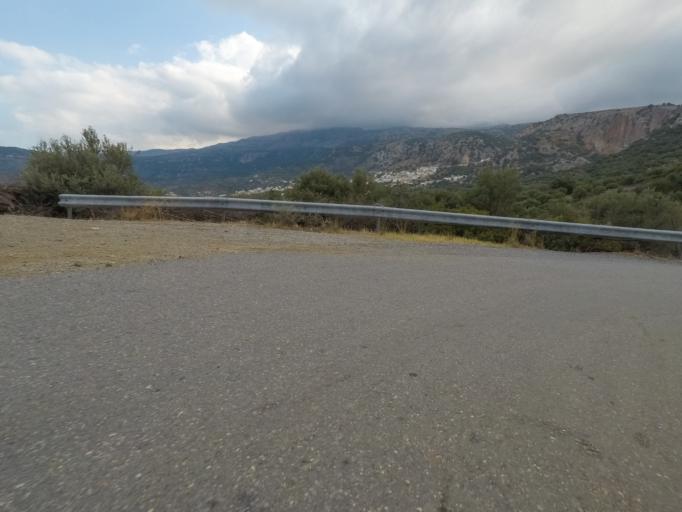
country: GR
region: Crete
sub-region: Nomos Lasithiou
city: Kritsa
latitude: 35.1659
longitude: 25.6557
